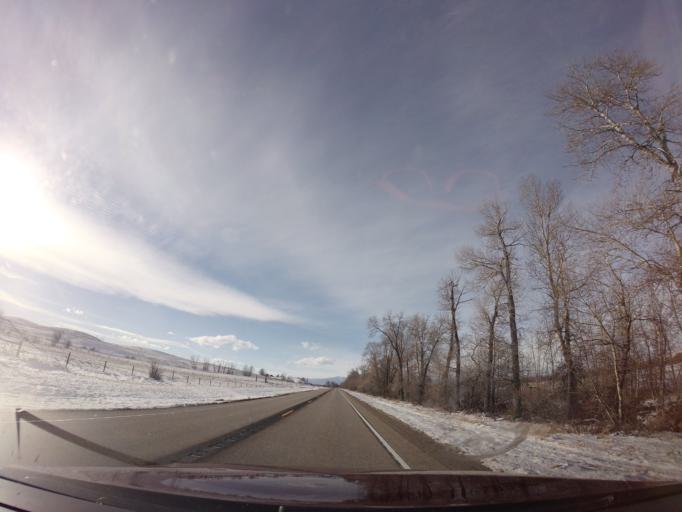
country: US
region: Montana
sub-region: Carbon County
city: Red Lodge
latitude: 45.4120
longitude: -109.1174
